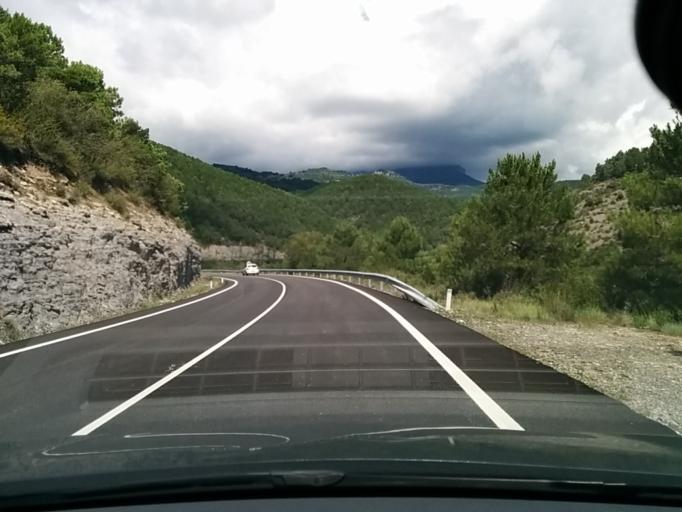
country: ES
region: Aragon
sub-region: Provincia de Huesca
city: Laspuna
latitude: 42.5162
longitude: 0.1431
